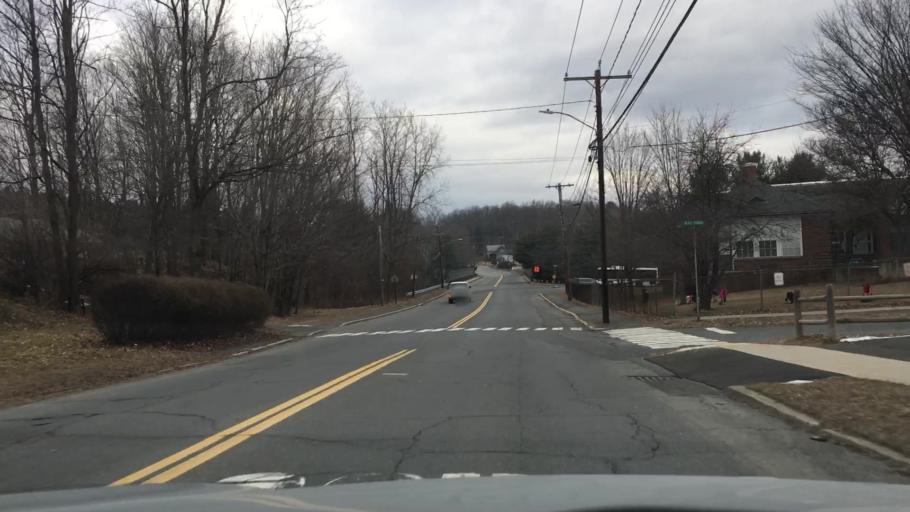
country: US
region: Massachusetts
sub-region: Franklin County
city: Greenfield
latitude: 42.6050
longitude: -72.6115
